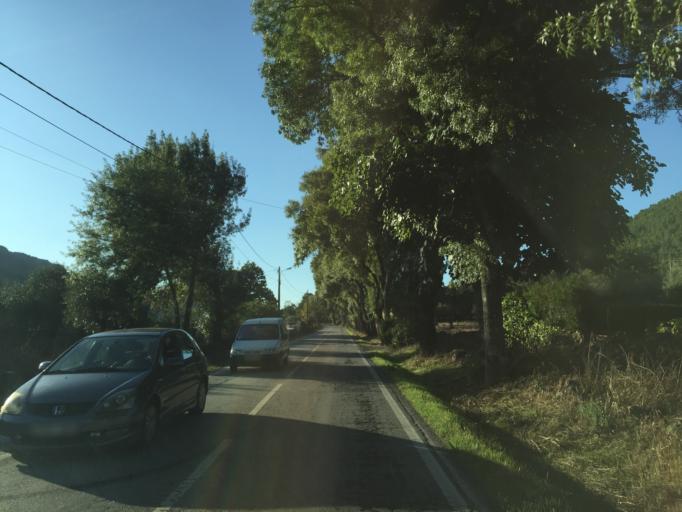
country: PT
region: Portalegre
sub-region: Marvao
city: Marvao
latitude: 39.3920
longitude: -7.4143
